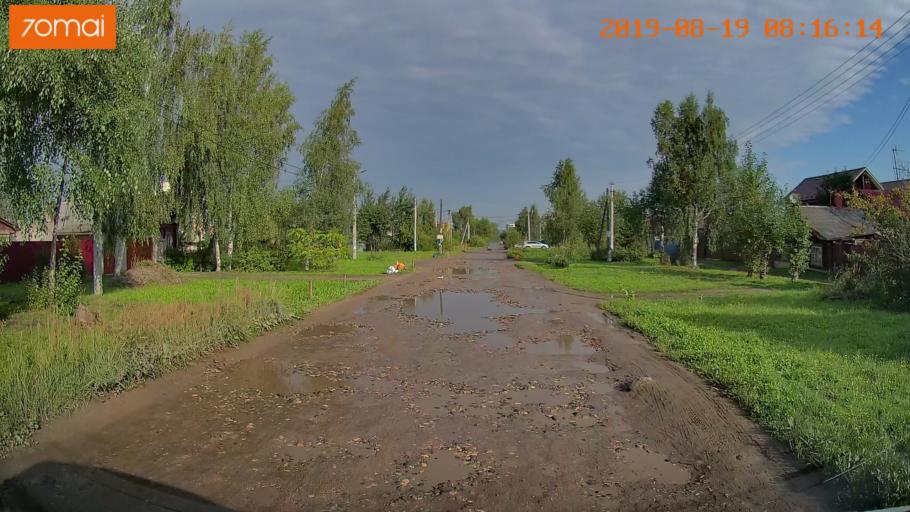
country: RU
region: Ivanovo
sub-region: Gorod Ivanovo
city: Ivanovo
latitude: 56.9744
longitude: 40.9993
